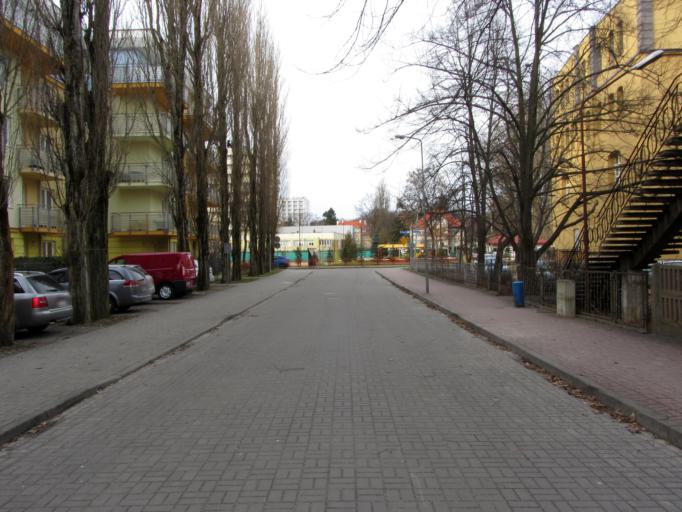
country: PL
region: West Pomeranian Voivodeship
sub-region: Powiat kolobrzeski
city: Kolobrzeg
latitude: 54.1821
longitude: 15.5821
